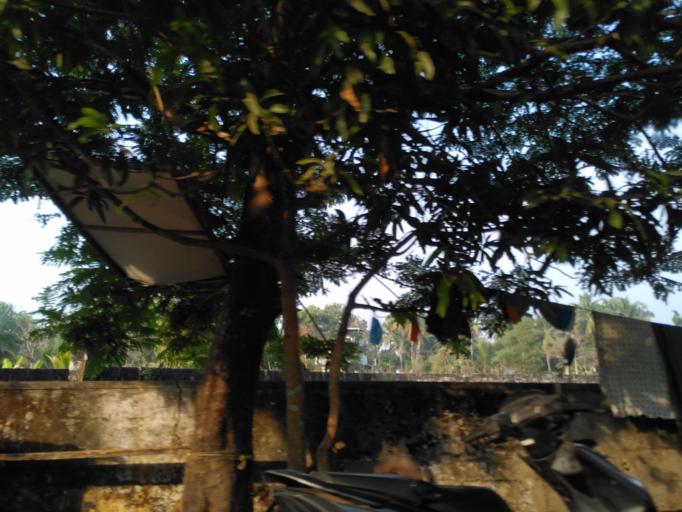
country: IN
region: Kerala
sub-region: Alappuzha
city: Arukutti
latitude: 9.9270
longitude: 76.3280
